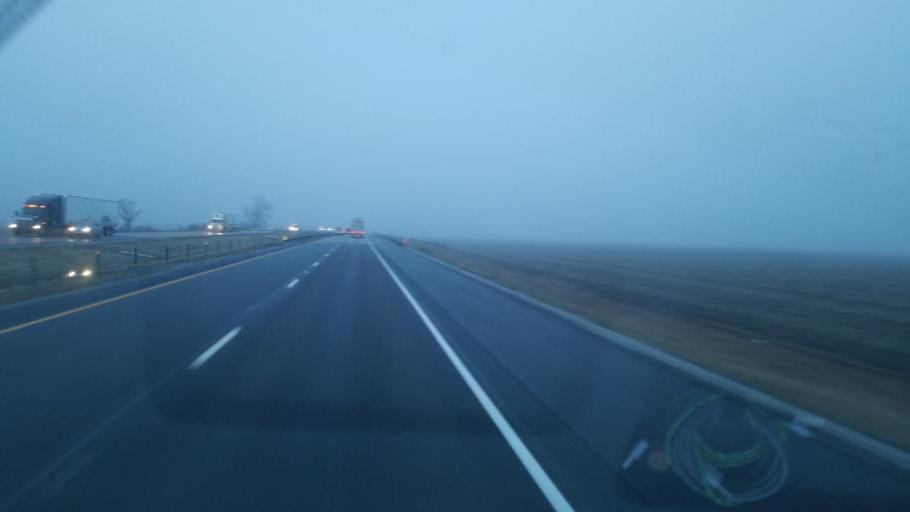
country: US
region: Indiana
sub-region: Newton County
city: Roselawn
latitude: 41.2357
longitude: -87.2953
